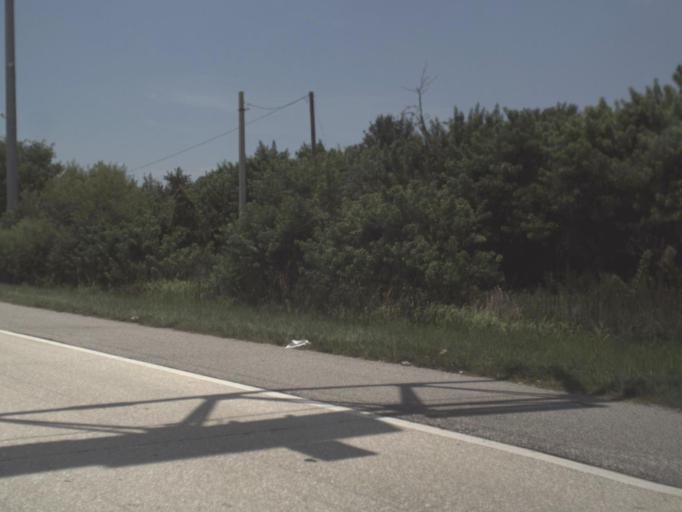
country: US
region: Florida
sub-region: Pinellas County
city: Pinellas Park
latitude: 27.8648
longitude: -82.6644
